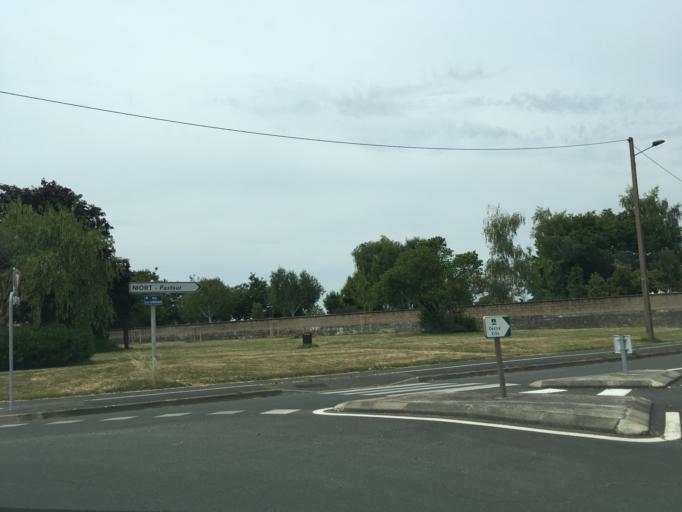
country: FR
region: Poitou-Charentes
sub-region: Departement des Deux-Sevres
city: Niort
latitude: 46.3096
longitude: -0.4724
